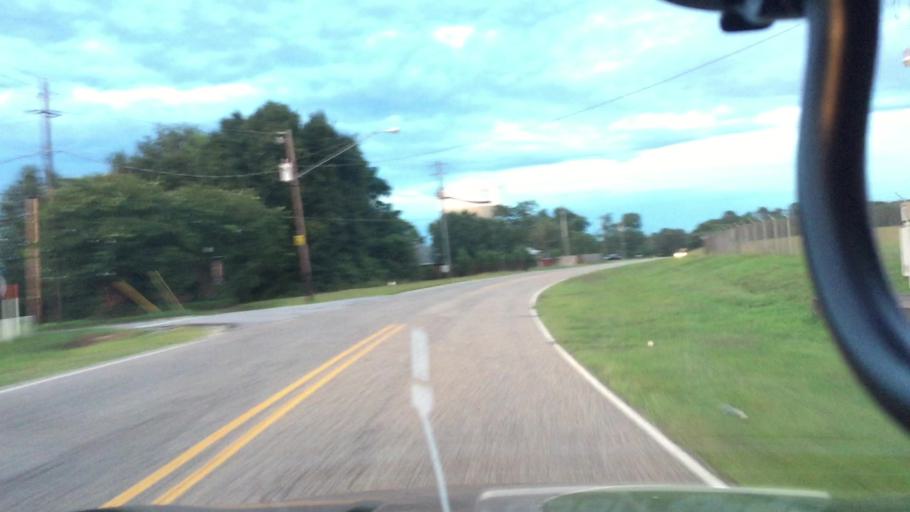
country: US
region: Alabama
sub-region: Coffee County
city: Enterprise
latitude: 31.3674
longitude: -85.8509
